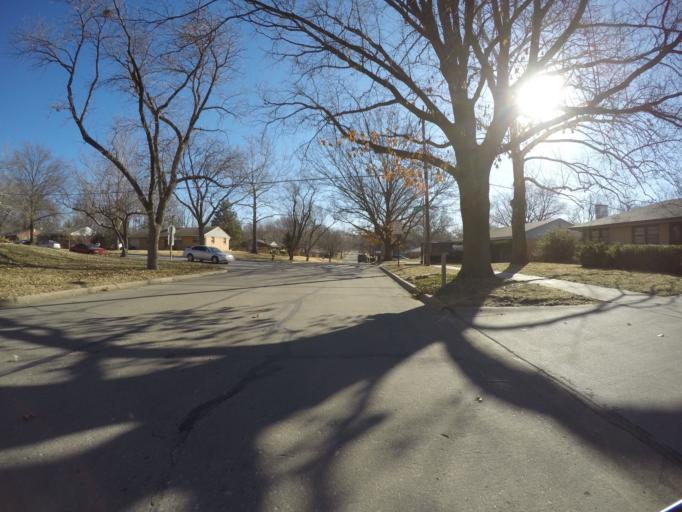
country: US
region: Kansas
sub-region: Riley County
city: Manhattan
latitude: 39.1987
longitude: -96.6046
